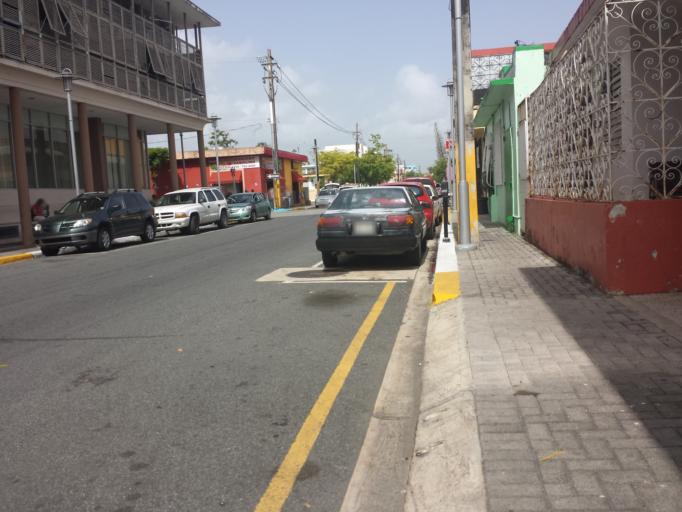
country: PR
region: Carolina
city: Carolina
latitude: 18.3831
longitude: -65.9566
